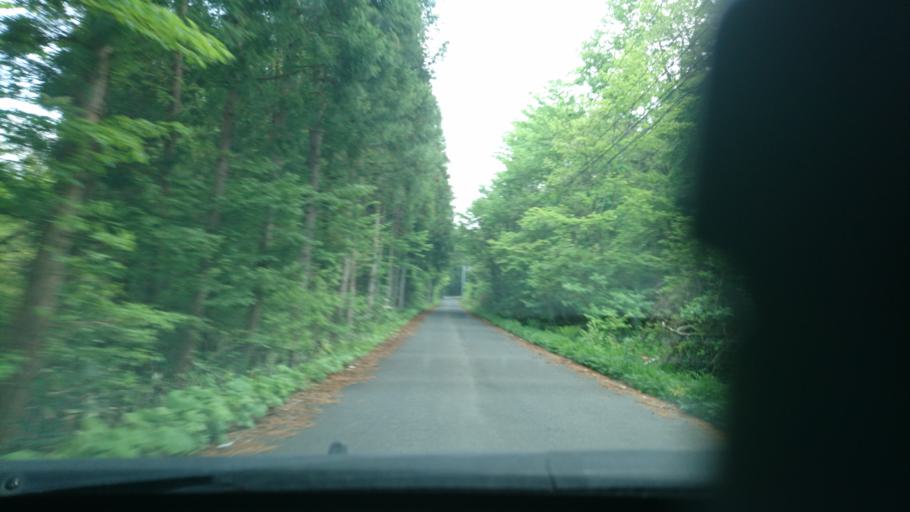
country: JP
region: Iwate
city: Ichinoseki
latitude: 38.9009
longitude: 140.9107
